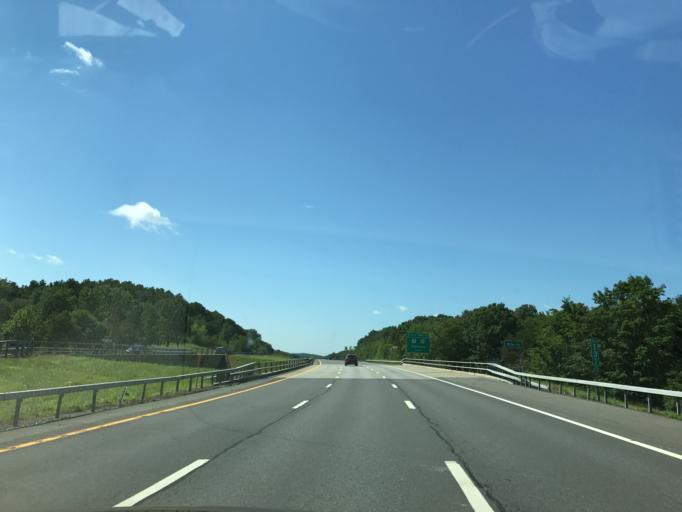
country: US
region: New York
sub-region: Rensselaer County
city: East Greenbush
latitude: 42.5806
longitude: -73.6792
